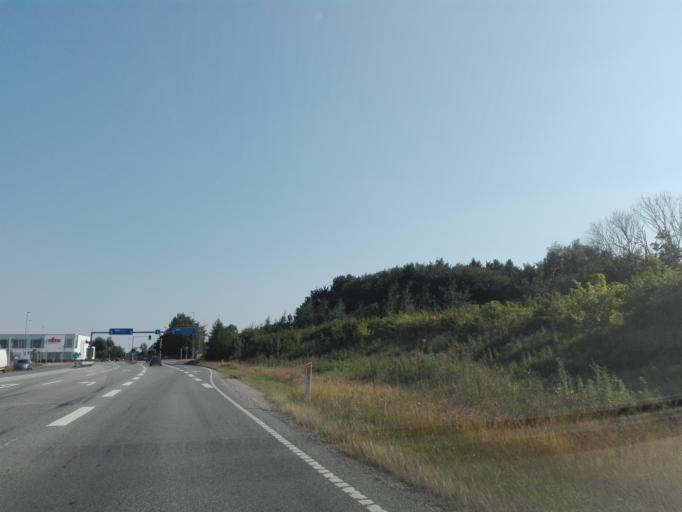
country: DK
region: Central Jutland
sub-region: Arhus Kommune
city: Tranbjerg
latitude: 56.1104
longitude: 10.1173
